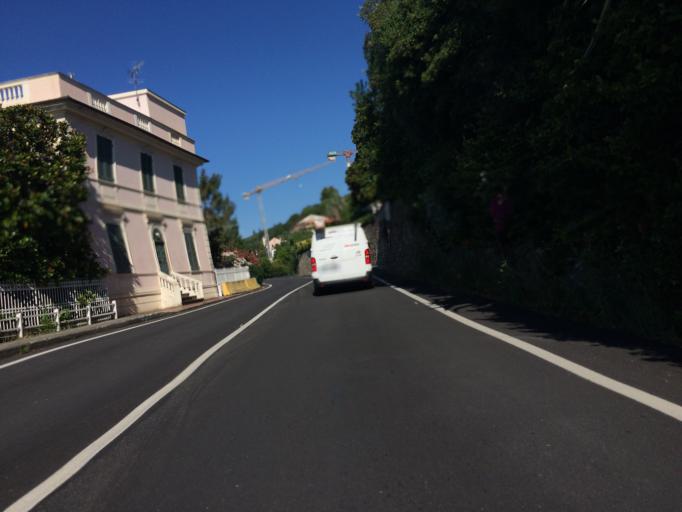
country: IT
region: Liguria
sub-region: Provincia di Genova
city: Santa Margherita Ligure
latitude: 44.3412
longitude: 9.2144
